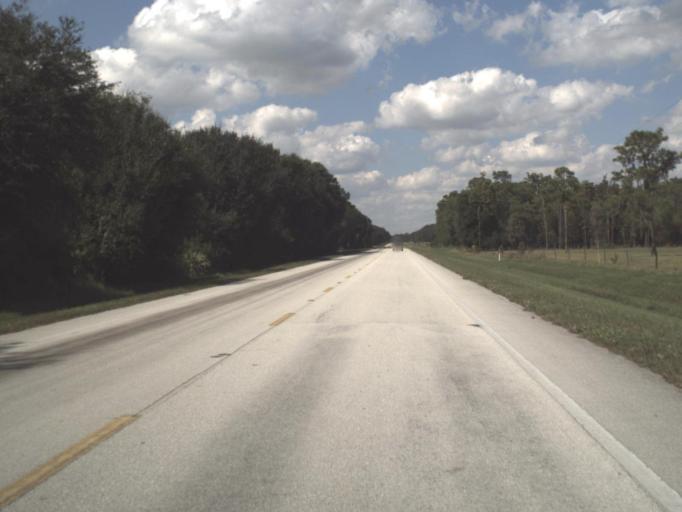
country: US
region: Florida
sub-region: Hardee County
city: Zolfo Springs
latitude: 27.4471
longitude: -81.6259
